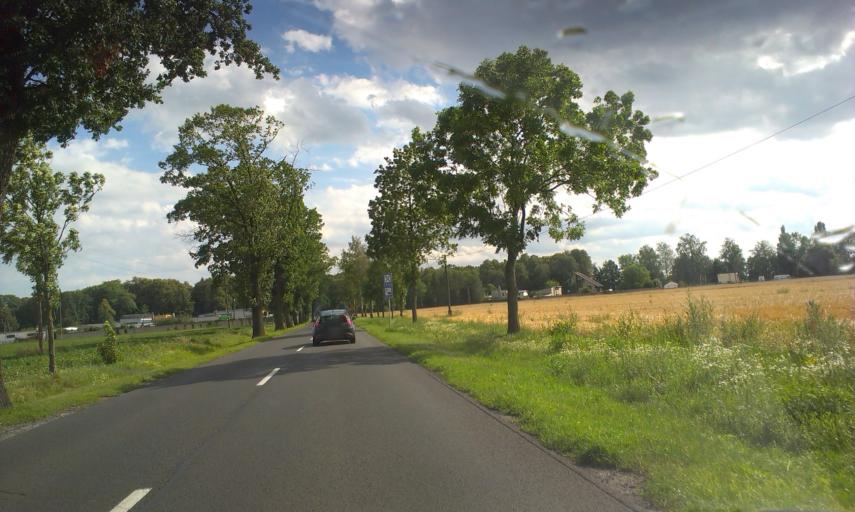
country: PL
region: Greater Poland Voivodeship
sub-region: Powiat zlotowski
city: Krajenka
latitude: 53.3062
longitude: 16.9885
